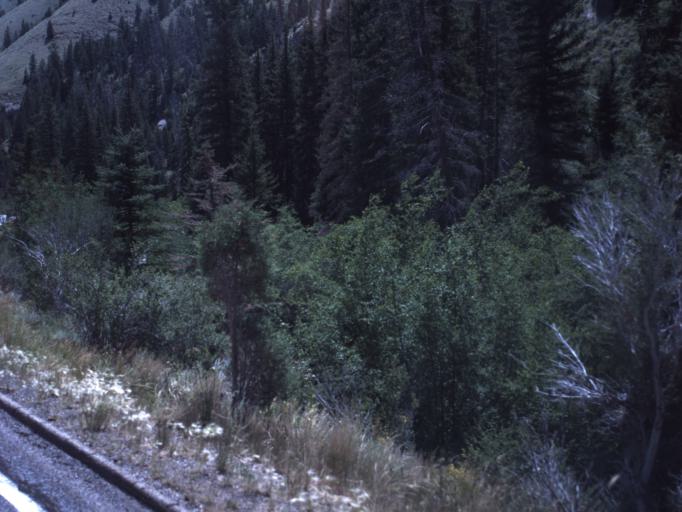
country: US
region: Utah
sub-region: Emery County
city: Huntington
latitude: 39.4749
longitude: -111.1565
